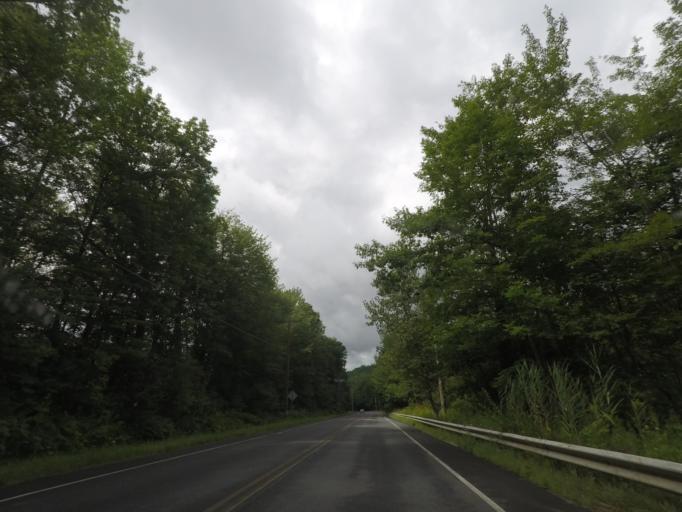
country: US
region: Massachusetts
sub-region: Berkshire County
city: Lanesborough
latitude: 42.5649
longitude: -73.2831
